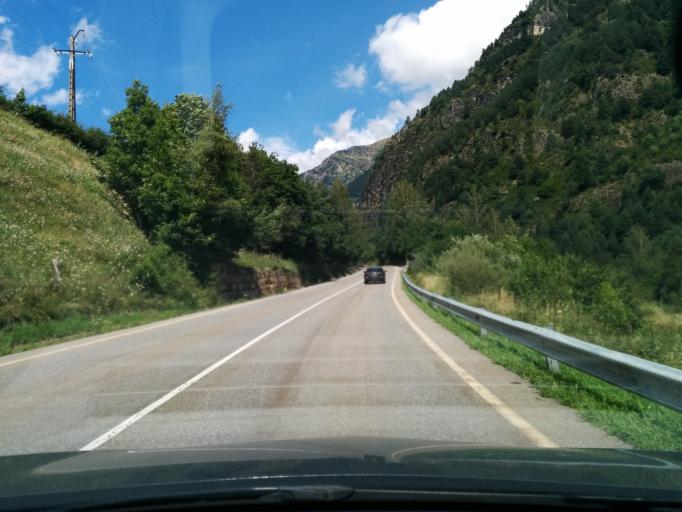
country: ES
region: Aragon
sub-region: Provincia de Huesca
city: Bielsa
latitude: 42.6553
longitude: 0.2083
